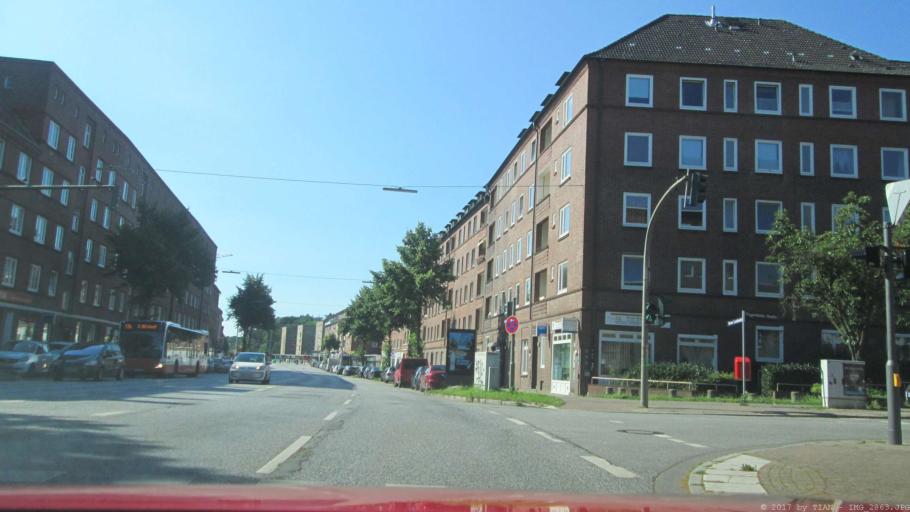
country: DE
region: Hamburg
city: Marienthal
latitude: 53.5490
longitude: 10.0816
